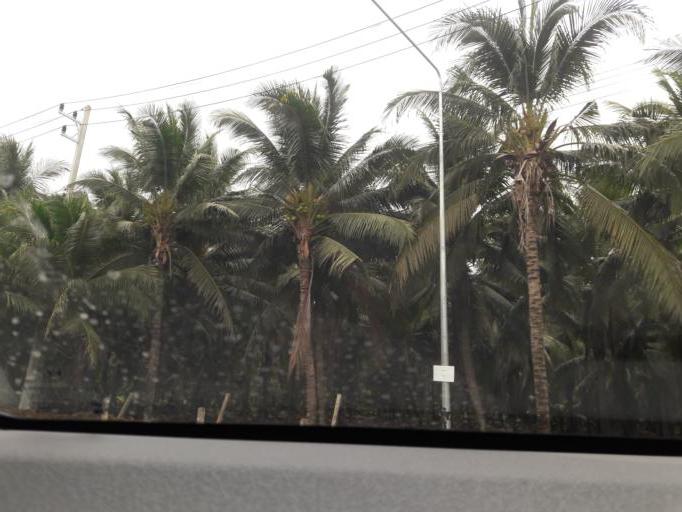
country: TH
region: Ratchaburi
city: Damnoen Saduak
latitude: 13.5744
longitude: 99.9865
